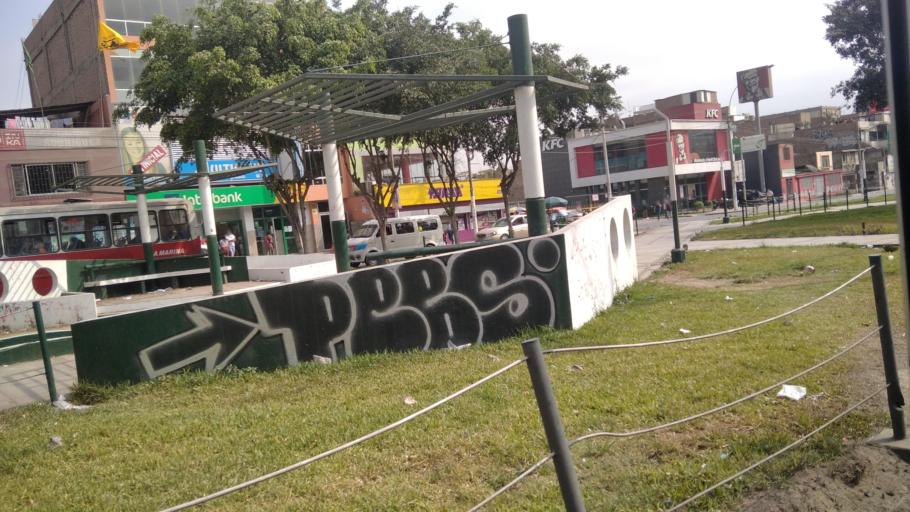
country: PE
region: Lima
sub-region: Lima
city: Independencia
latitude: -11.9690
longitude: -77.0050
